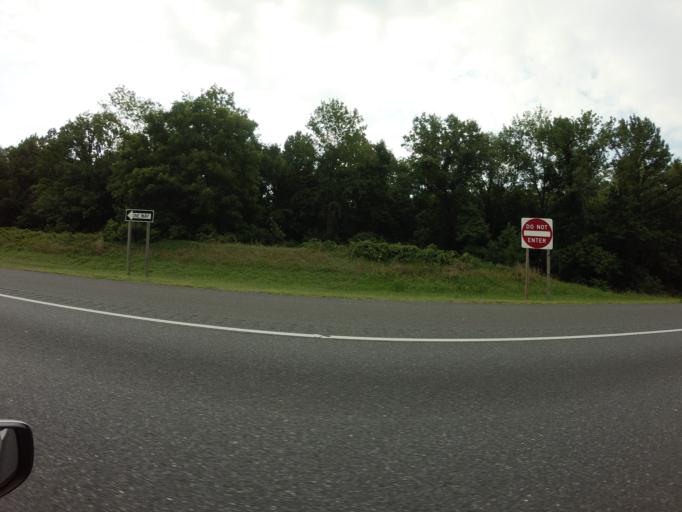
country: US
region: Maryland
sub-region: Baltimore County
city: White Marsh
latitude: 39.4113
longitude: -76.4124
